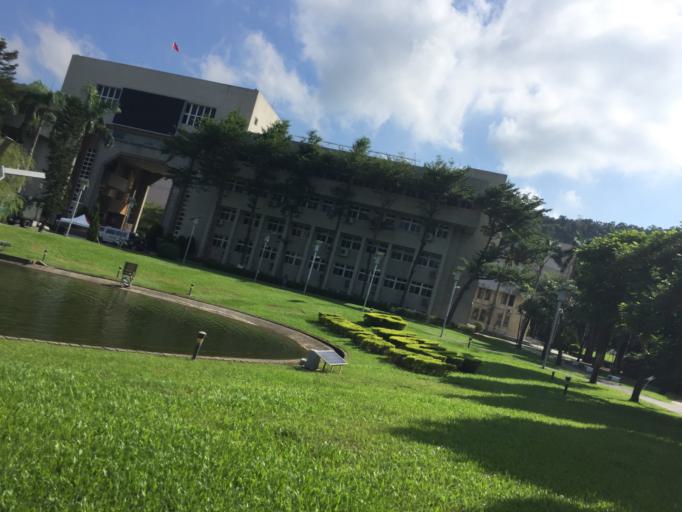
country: TW
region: Taiwan
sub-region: Changhua
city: Chang-hua
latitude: 24.0824
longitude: 120.5581
